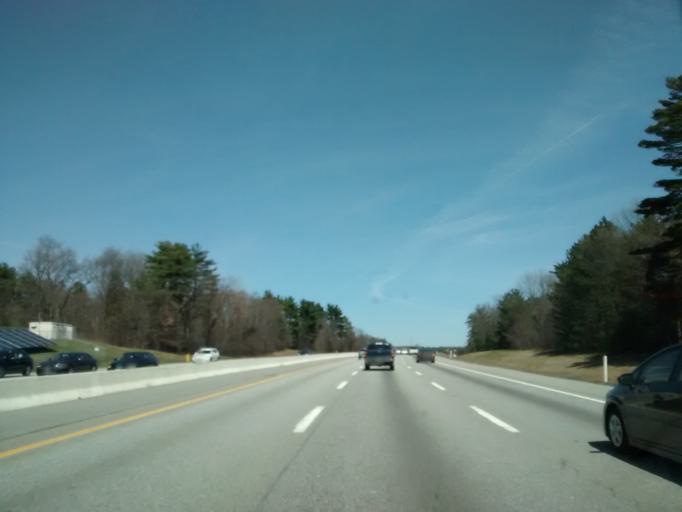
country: US
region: Massachusetts
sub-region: Middlesex County
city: Cochituate
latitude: 42.3265
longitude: -71.3334
